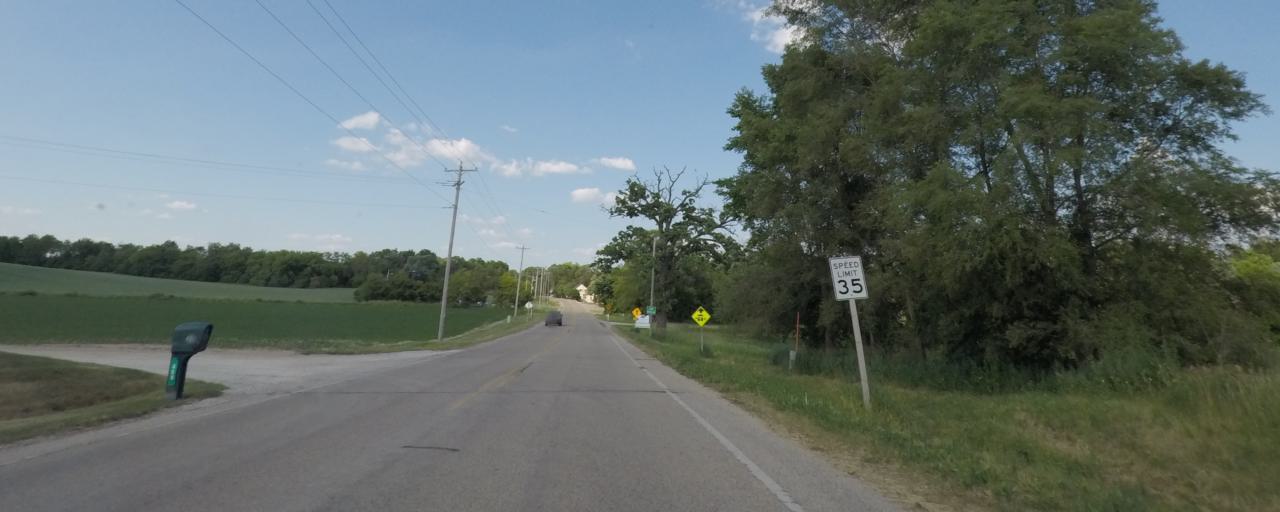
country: US
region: Wisconsin
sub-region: Walworth County
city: Potter Lake
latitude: 42.8199
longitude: -88.3247
